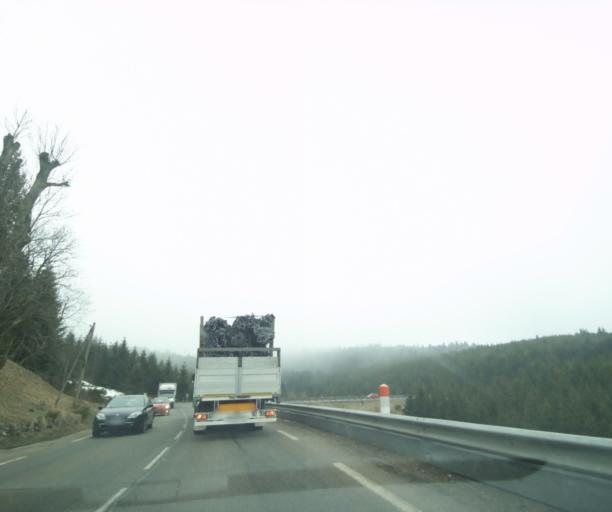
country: FR
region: Languedoc-Roussillon
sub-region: Departement de la Lozere
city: Langogne
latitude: 44.7108
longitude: 4.0087
